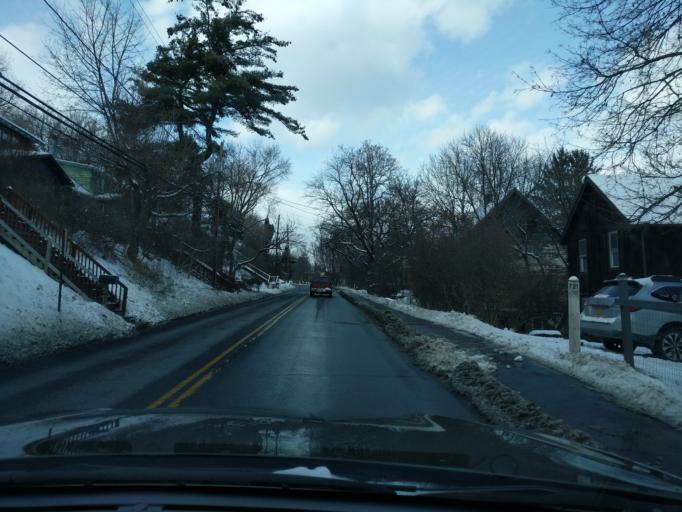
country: US
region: New York
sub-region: Tompkins County
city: Ithaca
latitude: 42.4485
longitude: -76.5172
